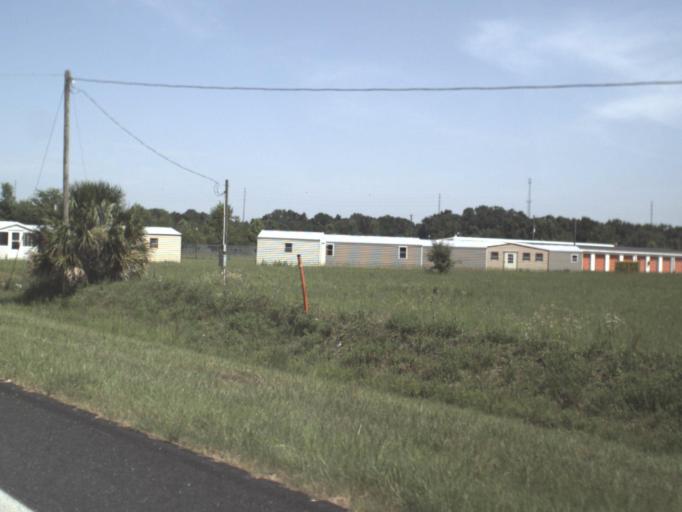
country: US
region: Florida
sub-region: Levy County
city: Manatee Road
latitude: 29.6001
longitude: -82.9769
